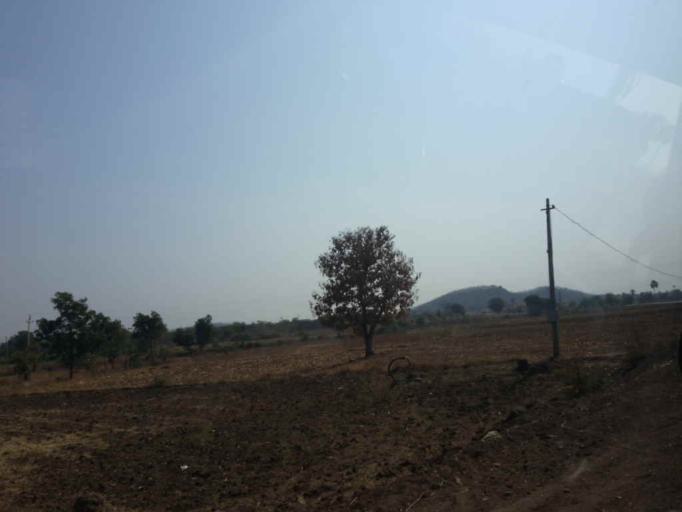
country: IN
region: Telangana
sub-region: Karimnagar
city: Koratla
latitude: 18.8616
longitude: 78.5872
